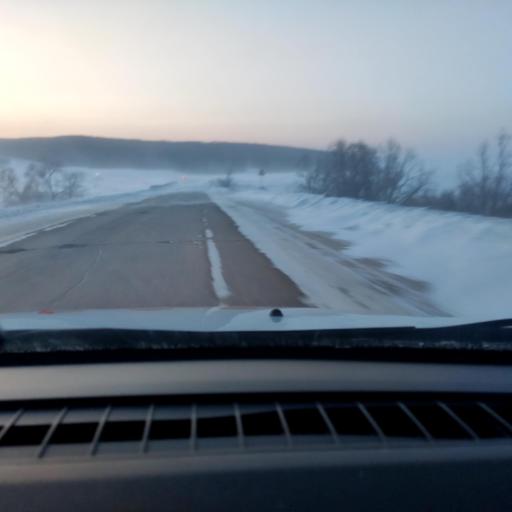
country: RU
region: Samara
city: Kinel'
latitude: 53.4412
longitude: 50.6555
